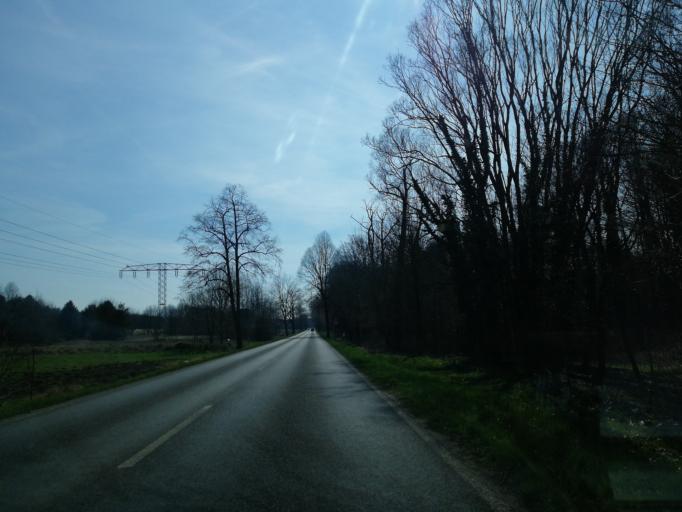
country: DE
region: Brandenburg
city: Altdobern
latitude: 51.6540
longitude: 14.0399
